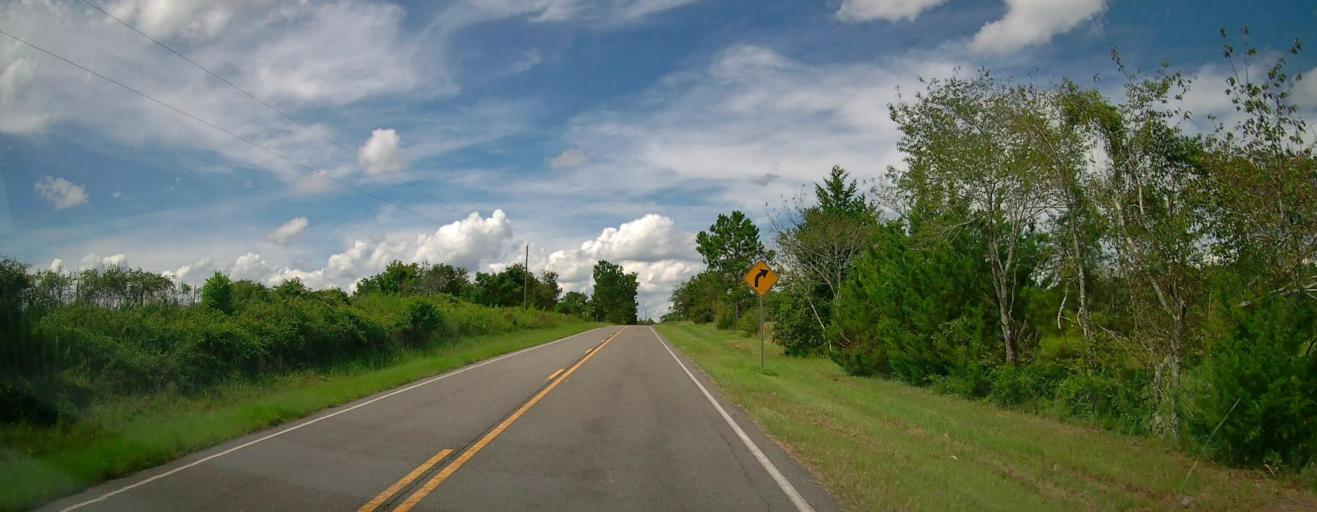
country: US
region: Georgia
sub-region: Taylor County
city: Butler
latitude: 32.4721
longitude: -84.2022
